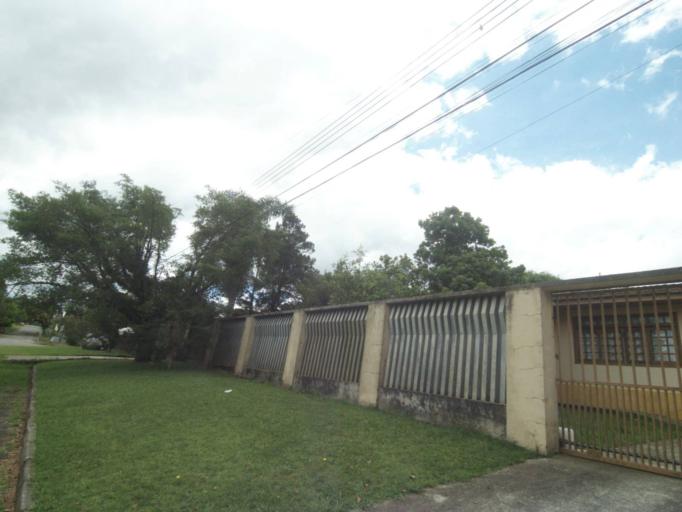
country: BR
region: Parana
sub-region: Curitiba
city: Curitiba
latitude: -25.4326
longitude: -49.3197
